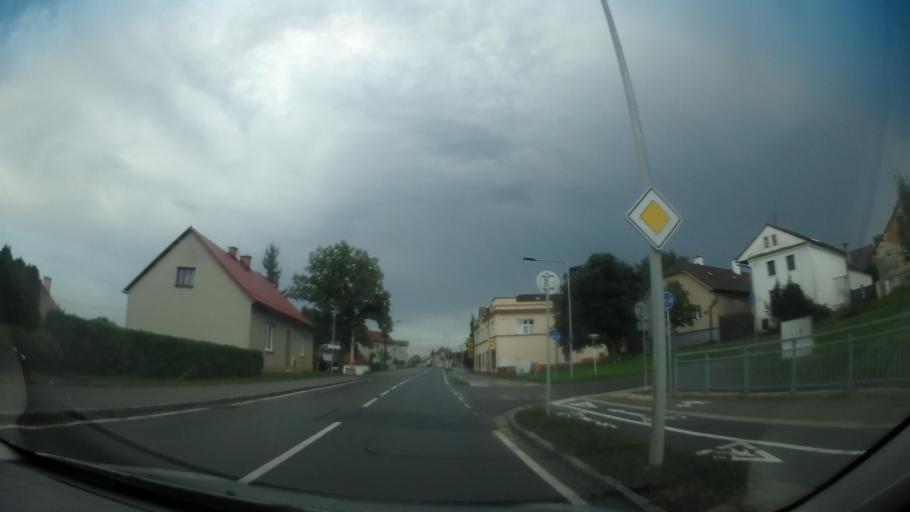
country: CZ
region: Olomoucky
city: Lostice
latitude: 49.7430
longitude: 16.9350
